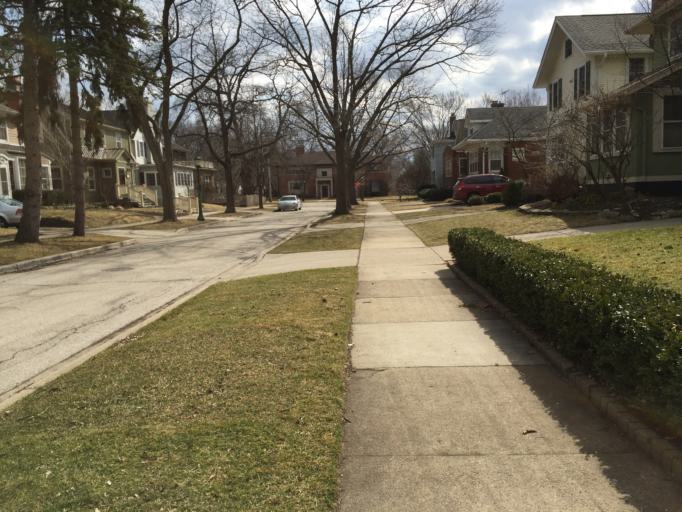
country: US
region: Illinois
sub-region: Cook County
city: Evanston
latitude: 42.0696
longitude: -87.6896
